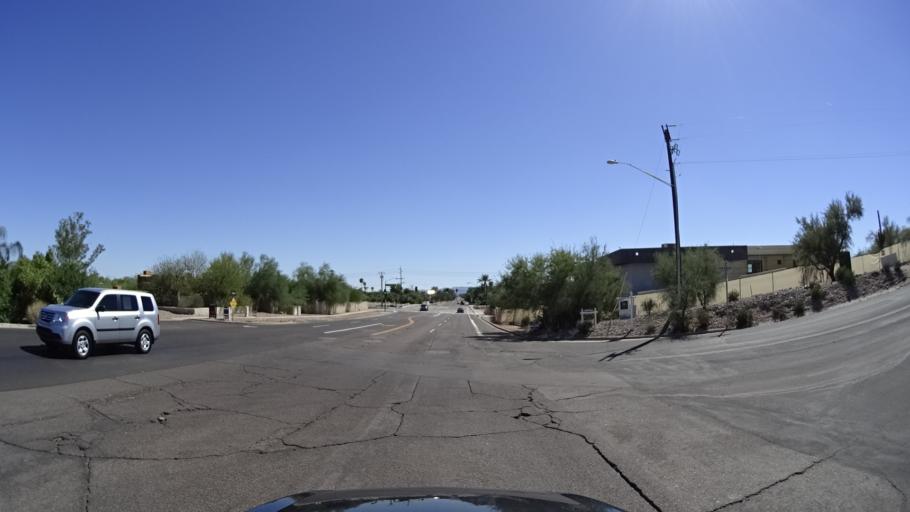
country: US
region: Arizona
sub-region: Maricopa County
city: Paradise Valley
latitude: 33.5198
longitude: -112.0130
